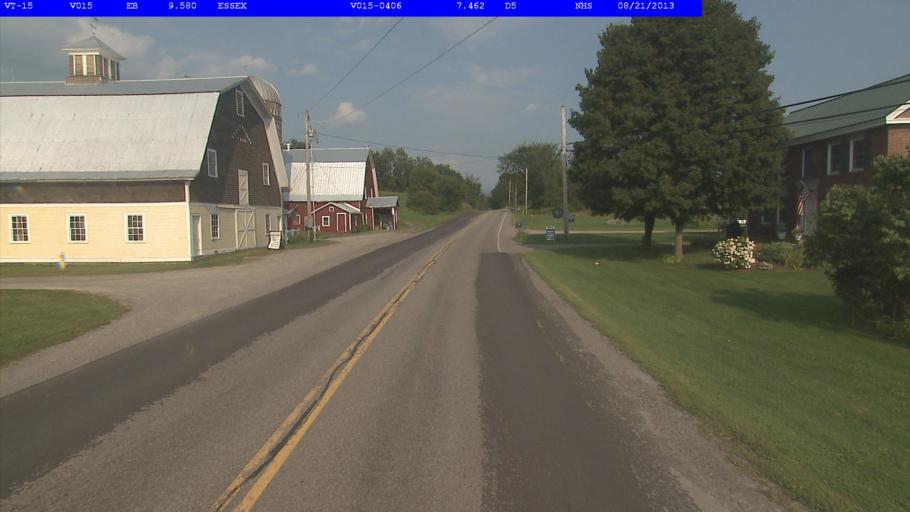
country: US
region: Vermont
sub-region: Chittenden County
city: Jericho
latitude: 44.5023
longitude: -73.0203
